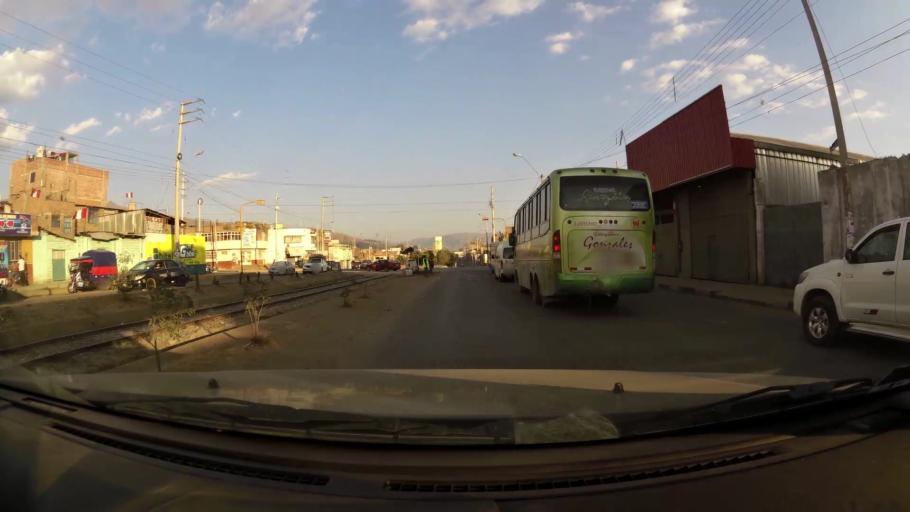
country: PE
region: Junin
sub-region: Provincia de Huancayo
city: El Tambo
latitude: -12.0511
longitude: -75.2149
